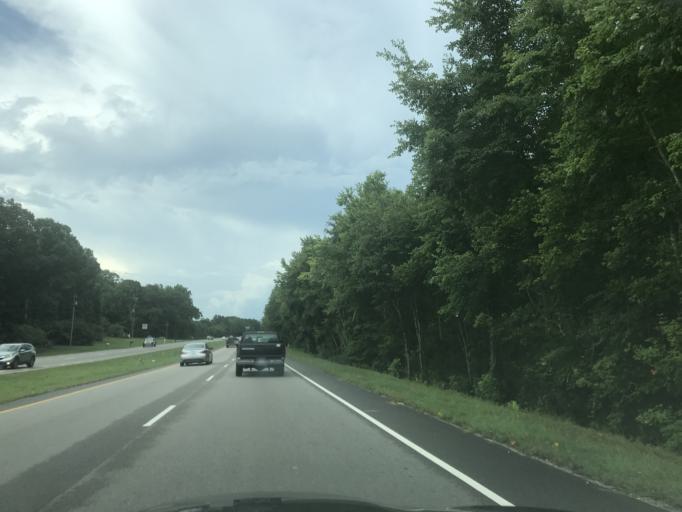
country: US
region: North Carolina
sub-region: Wake County
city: Garner
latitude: 35.6841
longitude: -78.5398
